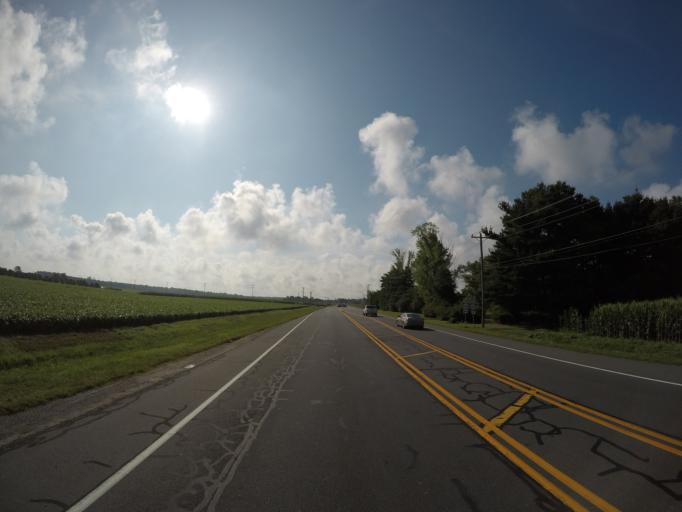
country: US
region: Delaware
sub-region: Sussex County
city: Bridgeville
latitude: 38.7548
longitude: -75.6296
